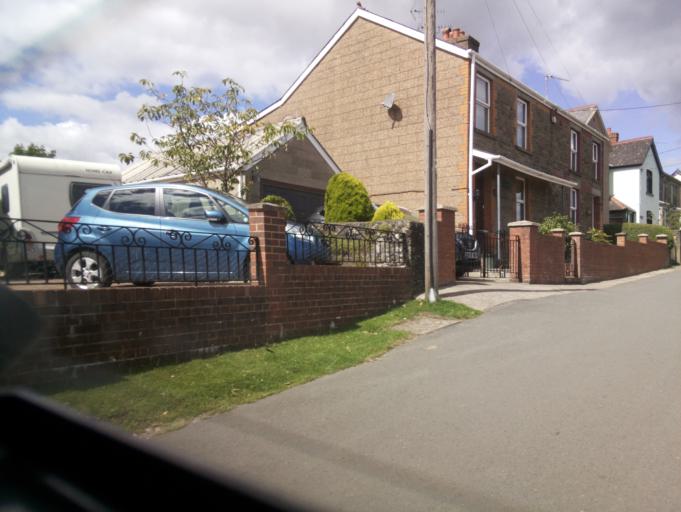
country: GB
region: England
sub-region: Gloucestershire
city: Bream
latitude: 51.7500
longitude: -2.5702
